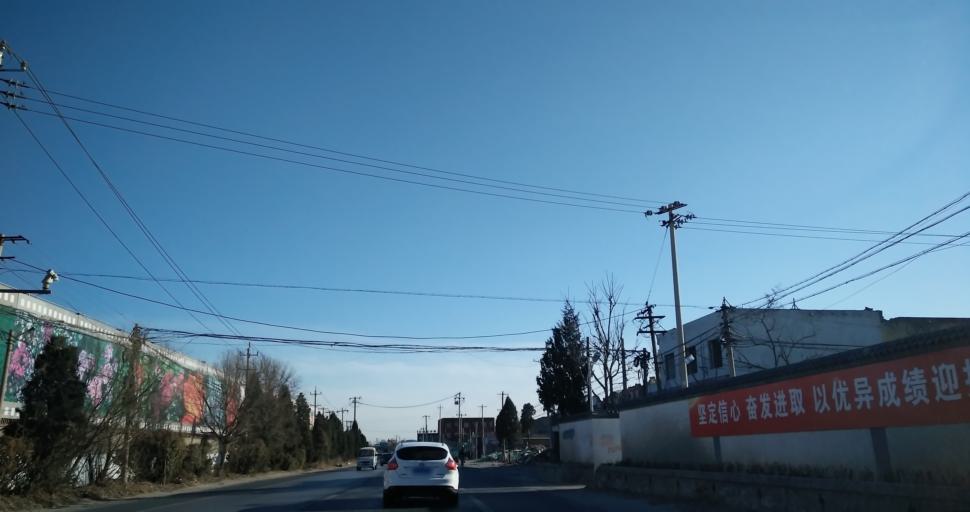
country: CN
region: Beijing
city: Yinghai
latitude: 39.7302
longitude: 116.4563
